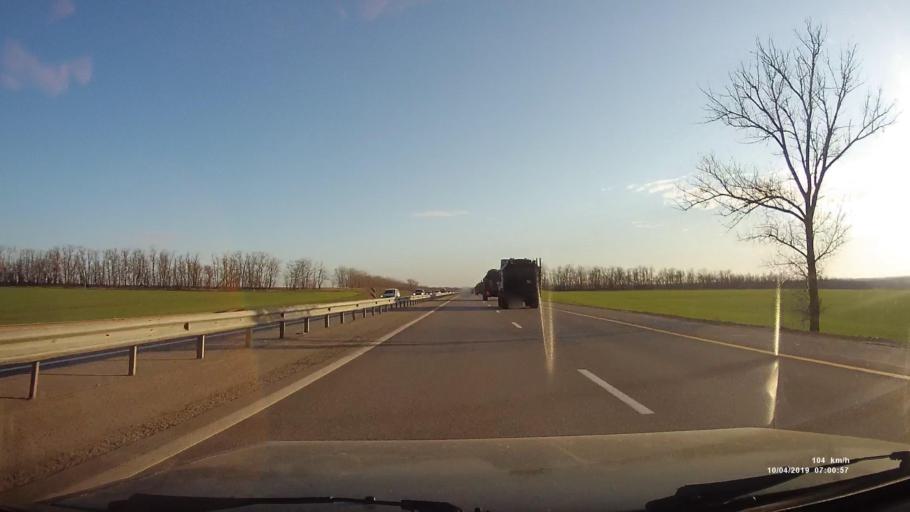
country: RU
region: Rostov
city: Krasyukovskaya
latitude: 47.5885
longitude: 39.9800
